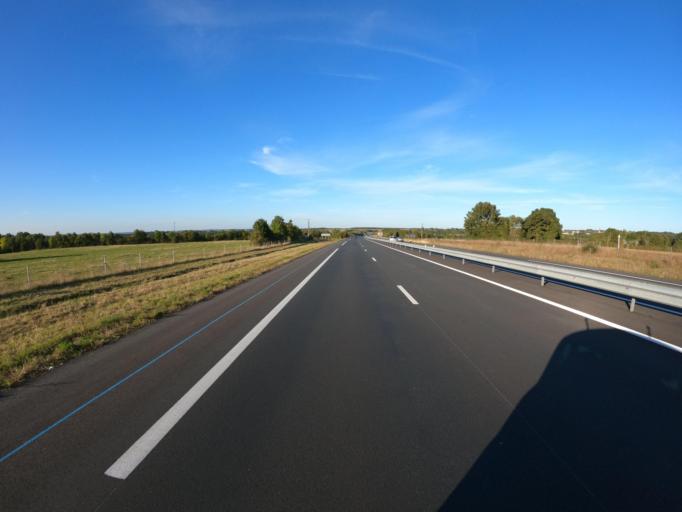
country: FR
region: Pays de la Loire
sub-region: Departement de la Vendee
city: Mortagne-sur-Sevre
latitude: 46.9898
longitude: -0.9157
